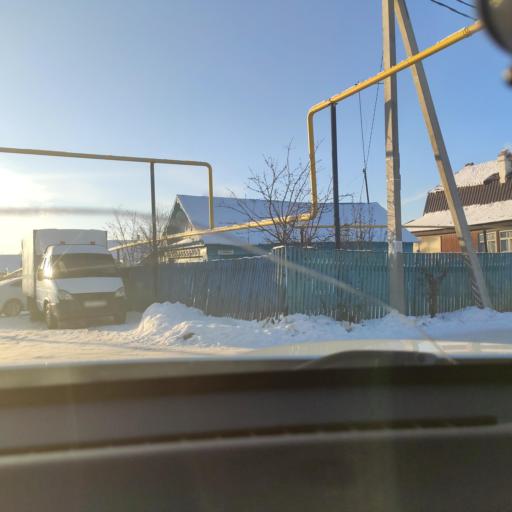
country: RU
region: Tatarstan
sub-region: Gorod Kazan'
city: Kazan
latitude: 55.7268
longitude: 49.1385
